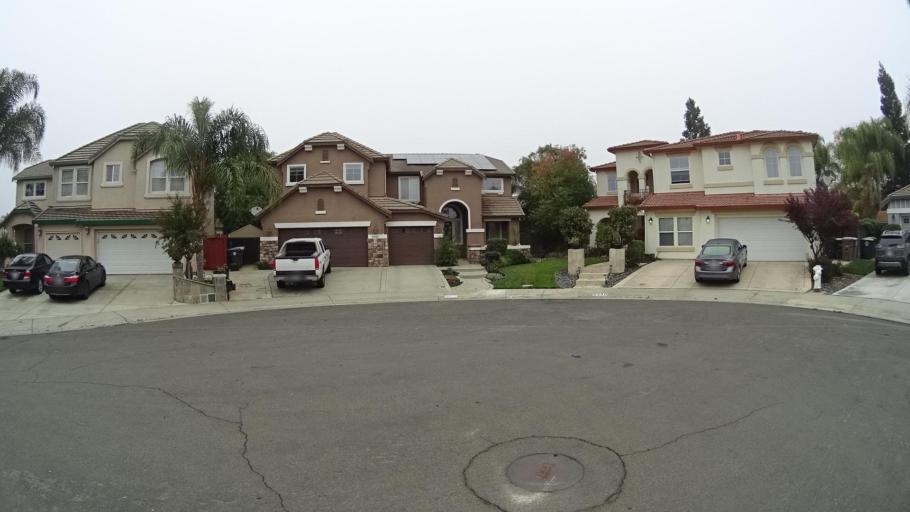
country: US
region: California
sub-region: Sacramento County
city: Elk Grove
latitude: 38.4145
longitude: -121.3453
